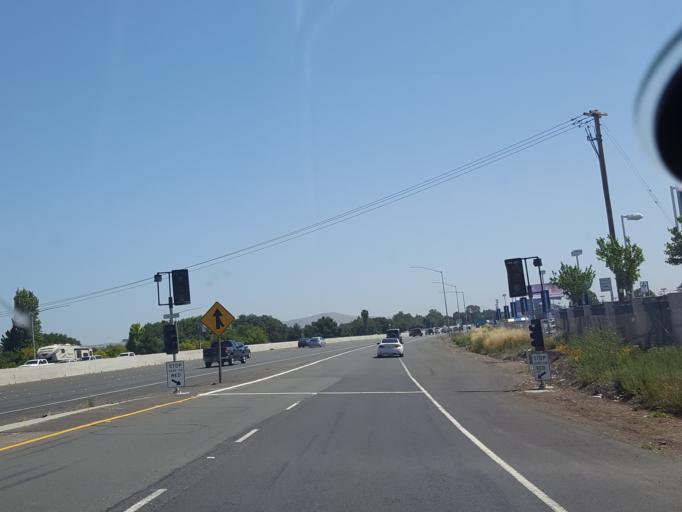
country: US
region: California
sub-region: Solano County
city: Suisun
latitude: 38.2427
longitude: -122.0850
